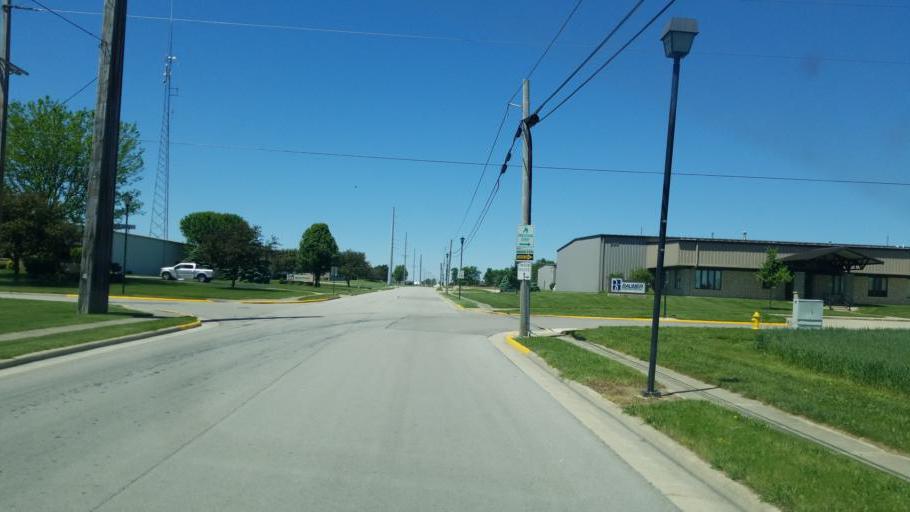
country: US
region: Ohio
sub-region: Auglaize County
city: Minster
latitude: 40.3857
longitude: -84.3856
